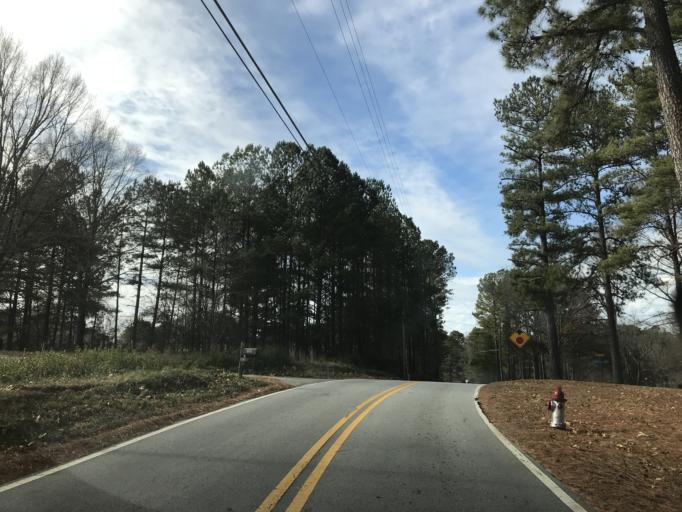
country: US
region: Georgia
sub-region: Douglas County
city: Douglasville
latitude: 33.7960
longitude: -84.8280
